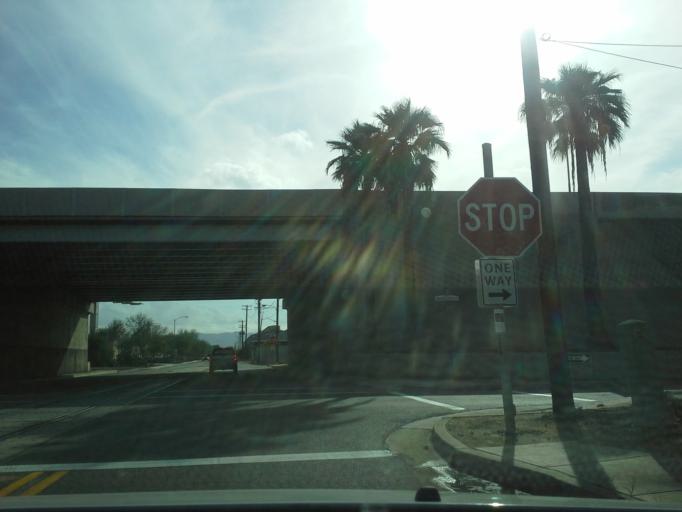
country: US
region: Arizona
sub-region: Maricopa County
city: Phoenix
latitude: 33.4301
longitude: -112.0869
